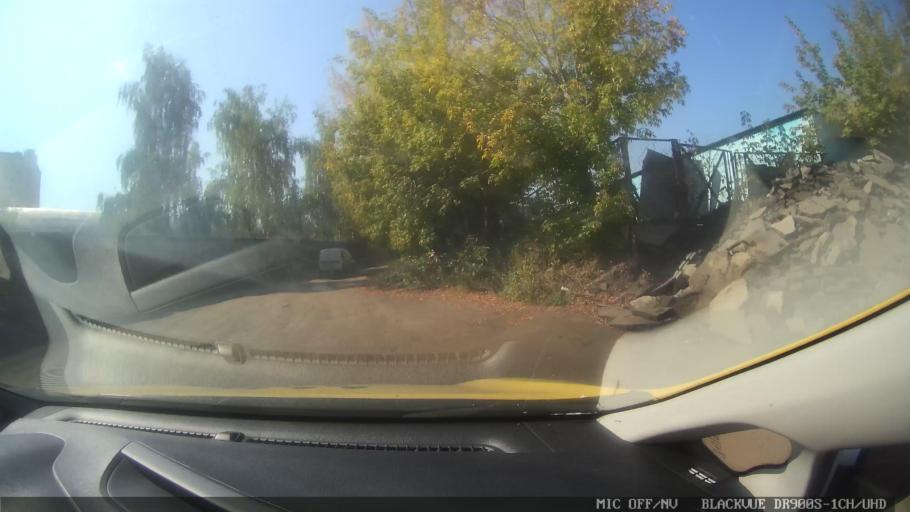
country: RU
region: Moscow
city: Bibirevo
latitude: 55.8806
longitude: 37.6112
